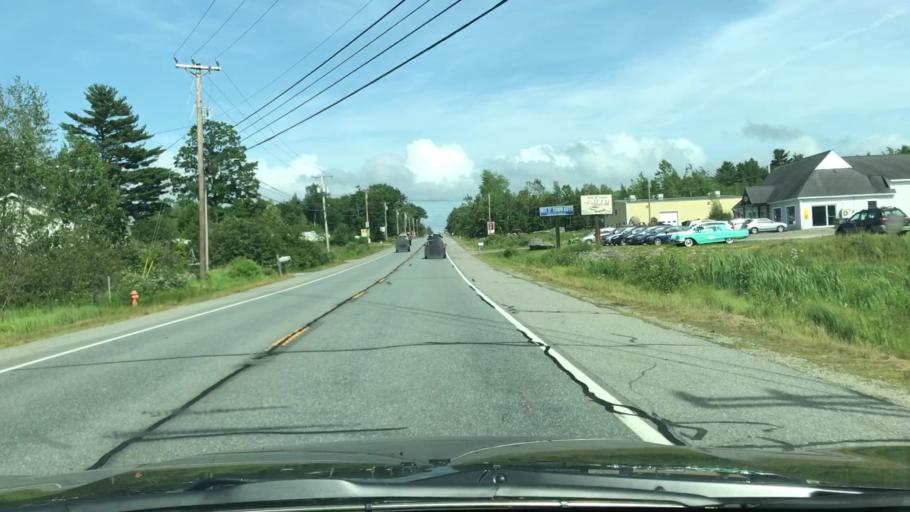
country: US
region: Maine
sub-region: Hancock County
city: Ellsworth
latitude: 44.5395
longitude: -68.4559
